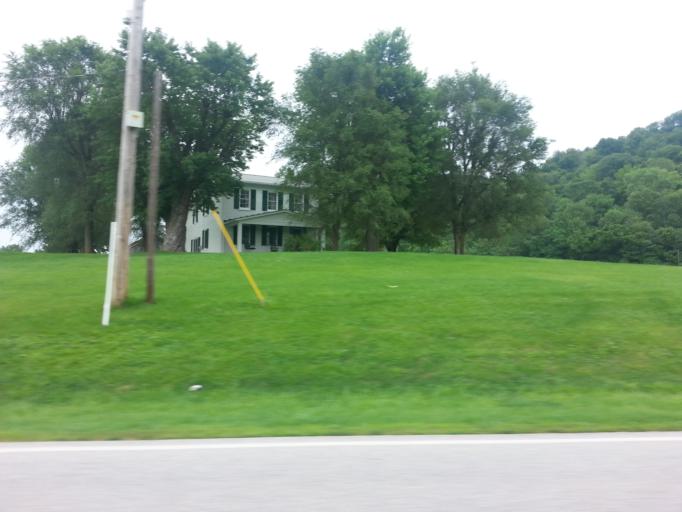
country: US
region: Ohio
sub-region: Brown County
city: Ripley
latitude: 38.7135
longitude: -83.8230
